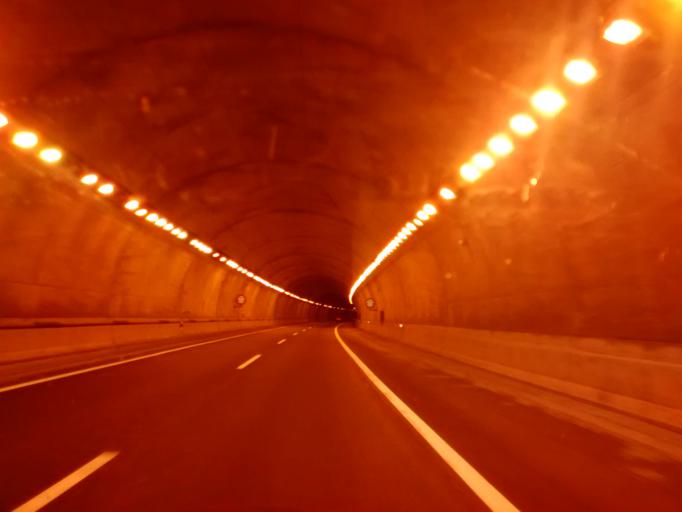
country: ES
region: Cantabria
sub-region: Provincia de Cantabria
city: Santiurde de Reinosa
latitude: 43.0523
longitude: -4.0866
